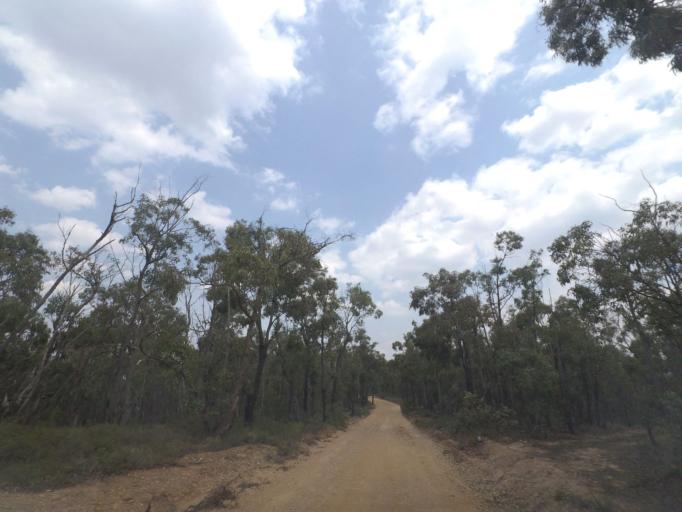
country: AU
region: Victoria
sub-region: Moorabool
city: Bacchus Marsh
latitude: -37.5792
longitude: 144.4411
